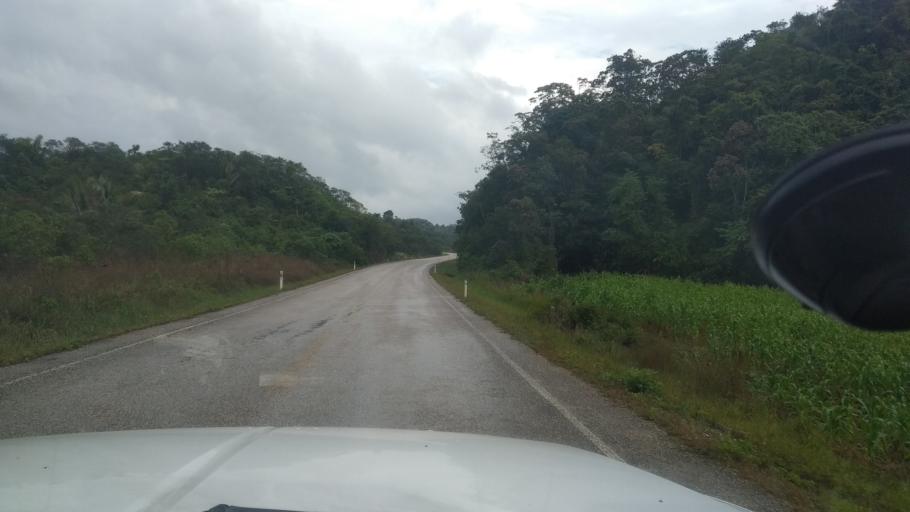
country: GT
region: Peten
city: San Luis
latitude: 16.1882
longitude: -89.1783
